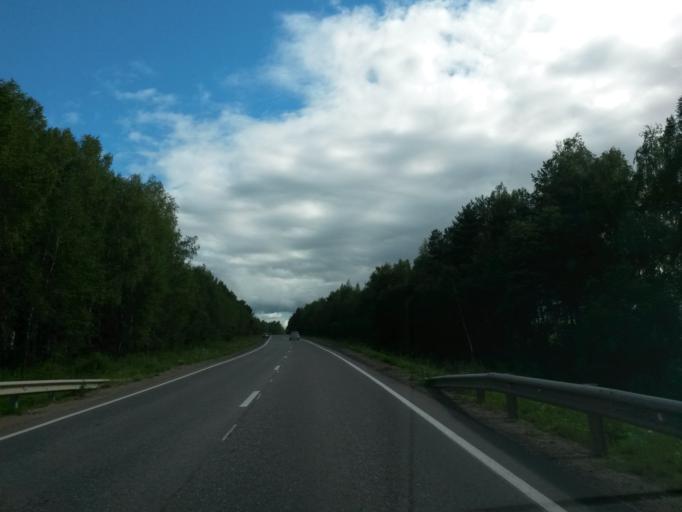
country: RU
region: Jaroslavl
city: Gavrilov-Yam
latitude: 57.3424
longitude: 39.9133
